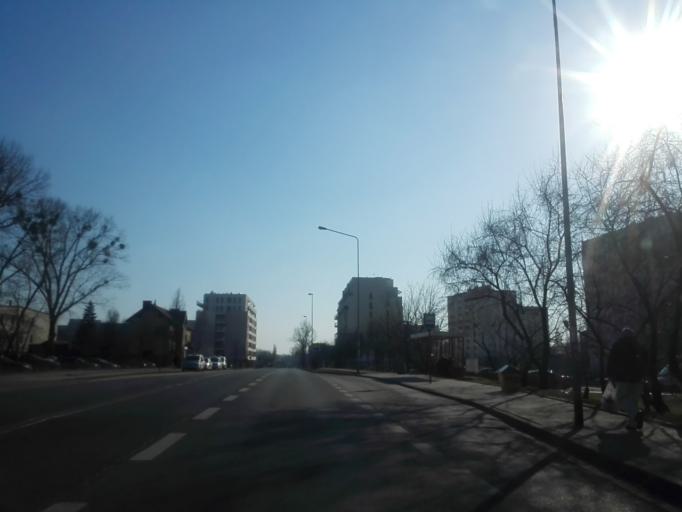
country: PL
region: Masovian Voivodeship
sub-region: Warszawa
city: Mokotow
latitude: 52.1739
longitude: 21.0121
